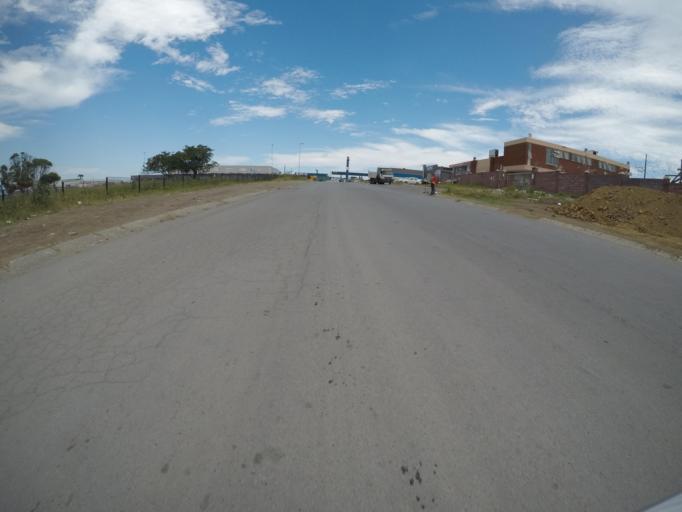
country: ZA
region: Eastern Cape
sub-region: Buffalo City Metropolitan Municipality
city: East London
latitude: -33.0336
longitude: 27.8811
